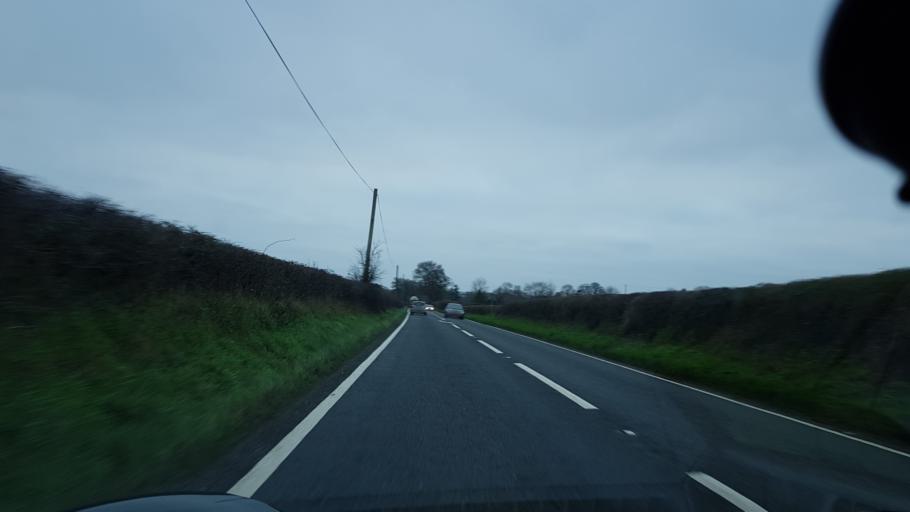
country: GB
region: England
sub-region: Somerset
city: Chard
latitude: 50.8996
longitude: -2.9483
